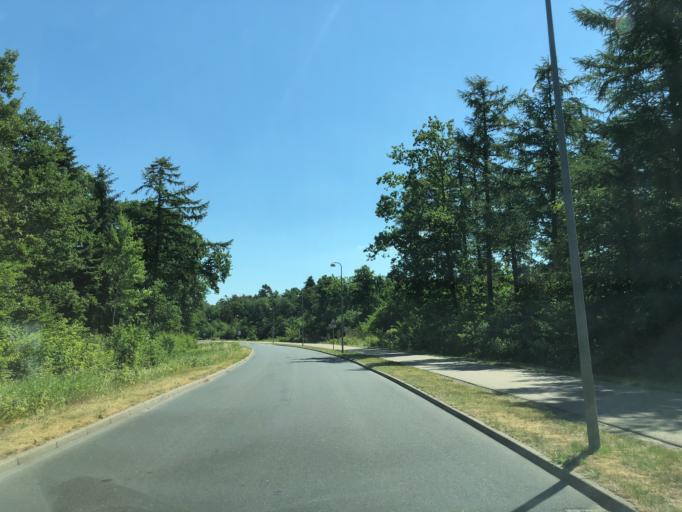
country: DK
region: Central Jutland
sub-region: Holstebro Kommune
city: Holstebro
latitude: 56.3610
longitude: 8.6861
